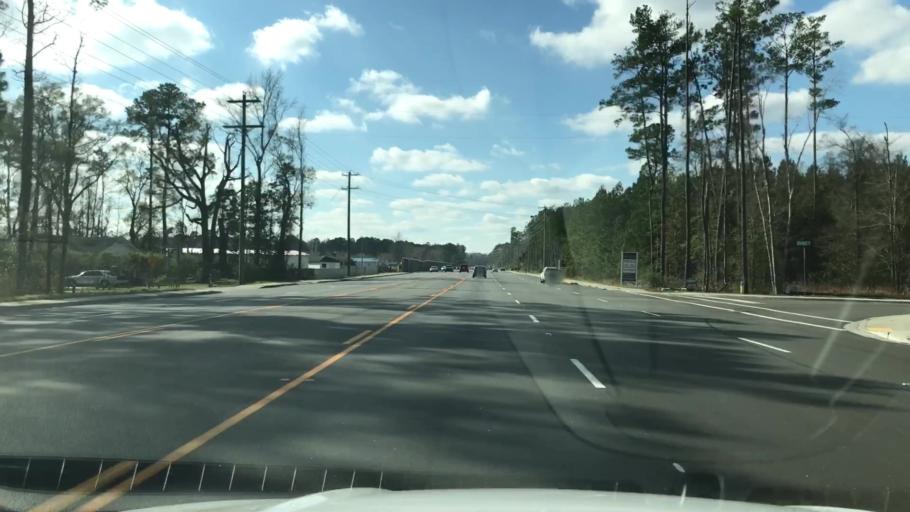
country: US
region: South Carolina
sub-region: Horry County
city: Socastee
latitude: 33.6479
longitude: -79.0242
